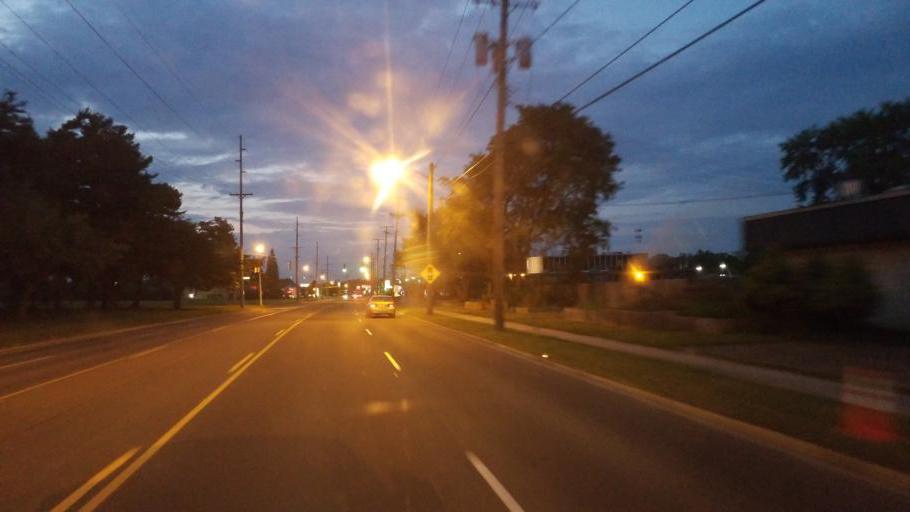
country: US
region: Ohio
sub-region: Trumbull County
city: Churchill
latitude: 41.1300
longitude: -80.6650
